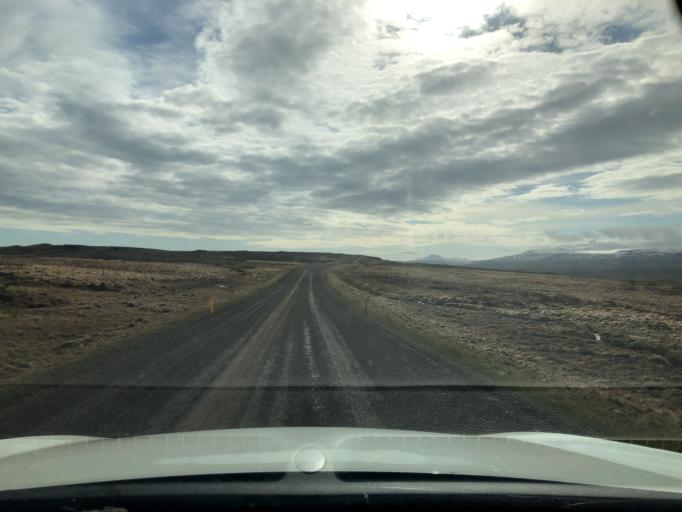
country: IS
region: West
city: Borgarnes
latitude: 65.0178
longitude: -22.0421
